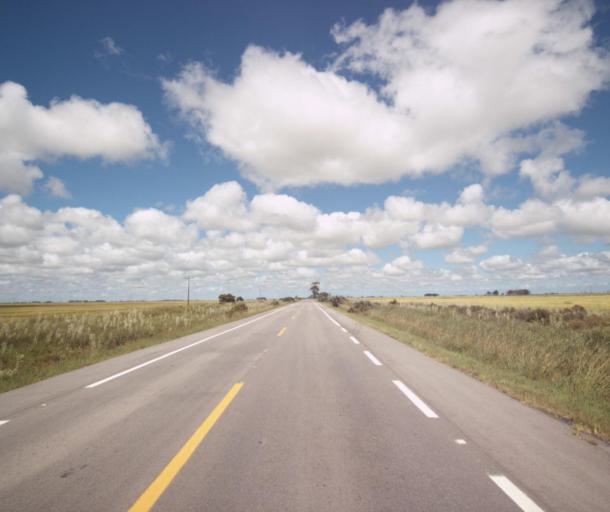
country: BR
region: Rio Grande do Sul
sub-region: Rio Grande
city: Rio Grande
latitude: -32.1514
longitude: -52.3921
